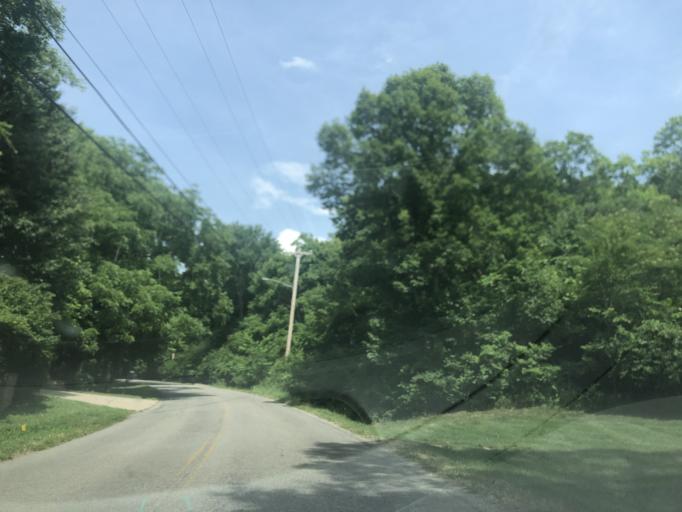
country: US
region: Tennessee
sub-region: Davidson County
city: Forest Hills
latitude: 36.0782
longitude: -86.8143
